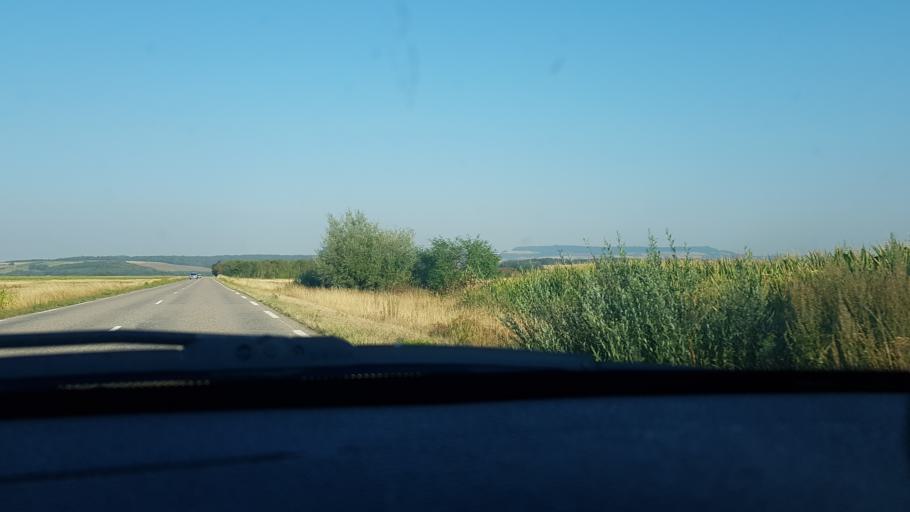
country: FR
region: Lorraine
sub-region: Departement des Vosges
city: Mirecourt
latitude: 48.3575
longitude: 6.1967
